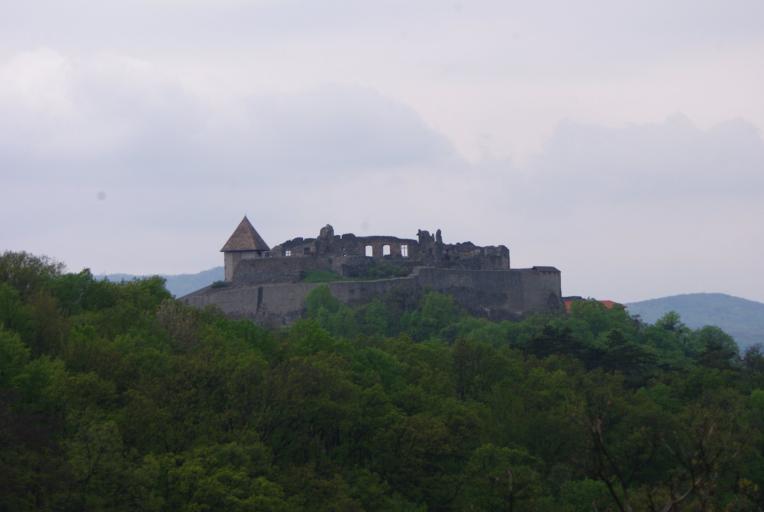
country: HU
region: Pest
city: Visegrad
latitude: 47.7950
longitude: 18.9881
